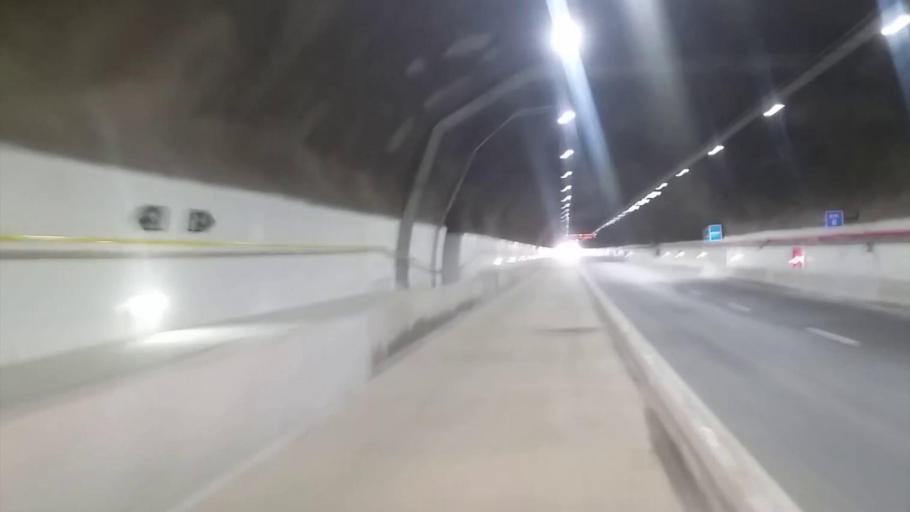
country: BR
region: Rio de Janeiro
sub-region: Nilopolis
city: Nilopolis
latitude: -22.9066
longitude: -43.3997
